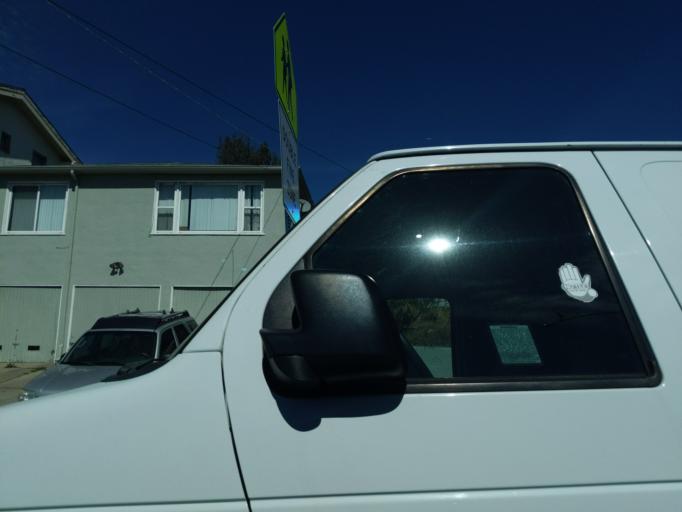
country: US
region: California
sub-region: Alameda County
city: Alameda
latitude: 37.7758
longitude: -122.2110
